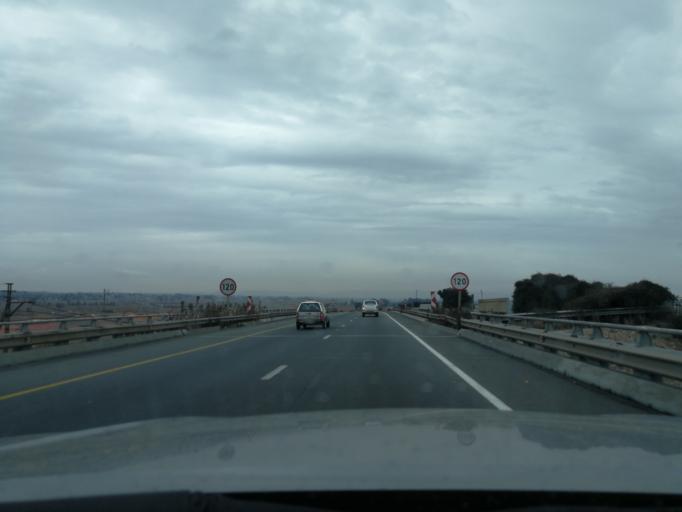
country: ZA
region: Gauteng
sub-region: Ekurhuleni Metropolitan Municipality
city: Germiston
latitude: -26.2916
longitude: 28.1552
